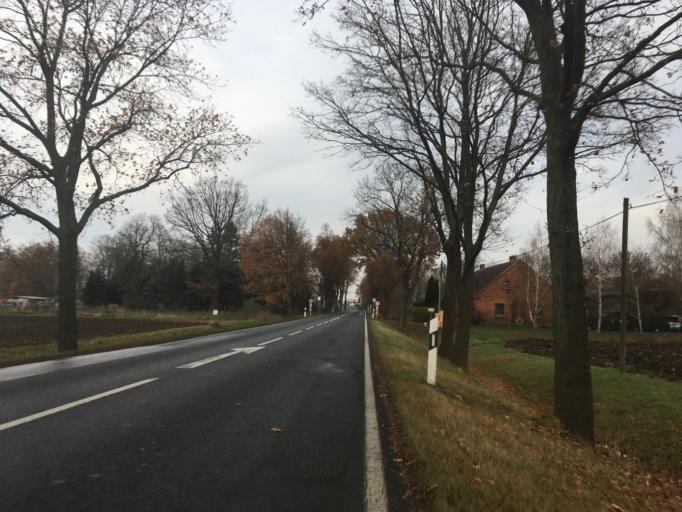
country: DE
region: Brandenburg
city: Letschin
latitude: 52.6272
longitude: 14.3524
